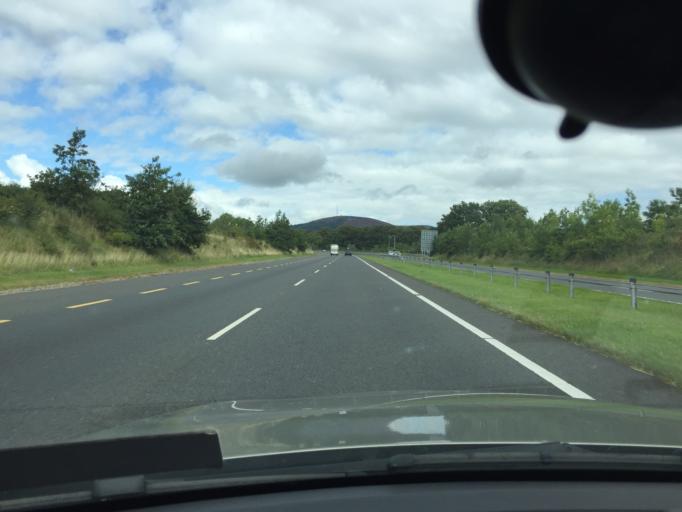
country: IE
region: Leinster
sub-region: Lu
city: Dundalk
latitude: 54.0463
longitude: -6.3646
